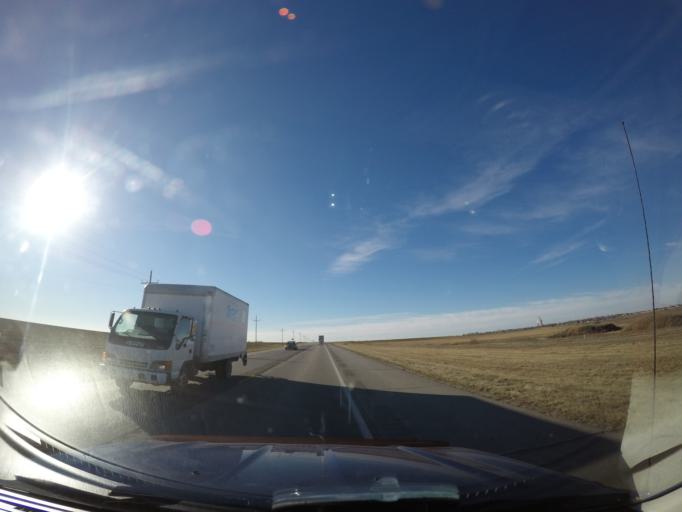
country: US
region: Kansas
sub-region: Marion County
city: Hillsboro
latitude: 38.3621
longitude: -97.2892
